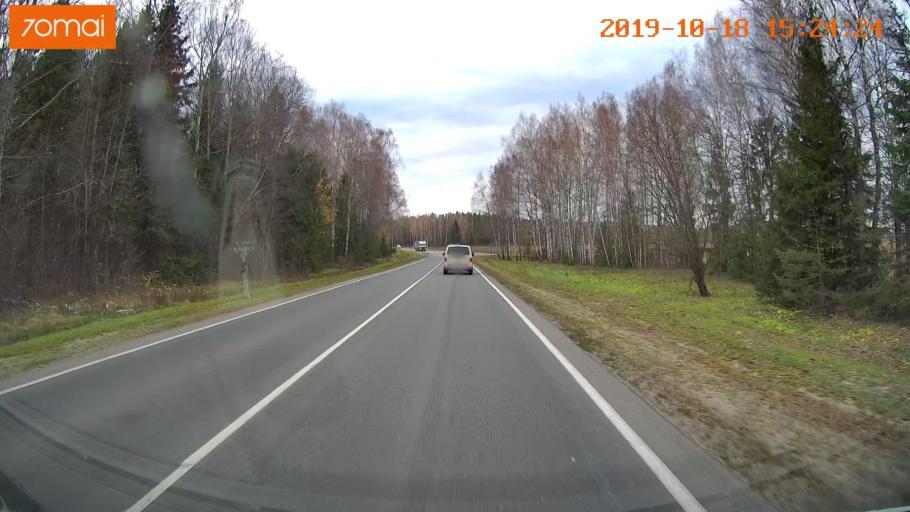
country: RU
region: Vladimir
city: Anopino
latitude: 55.7338
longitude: 40.7234
